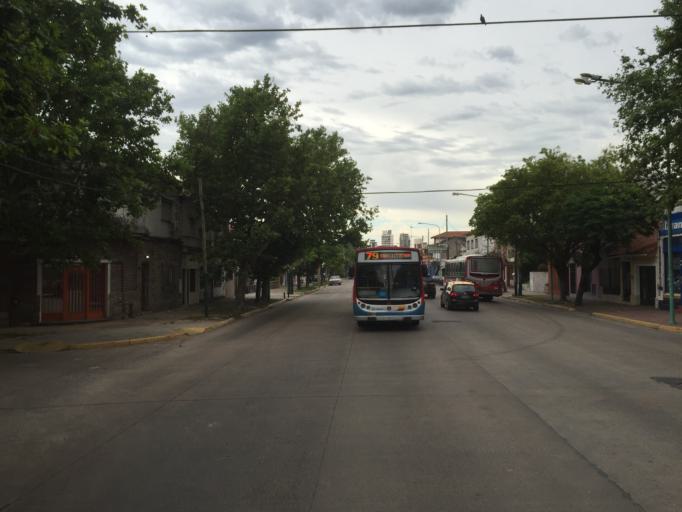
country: AR
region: Buenos Aires
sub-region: Partido de Lomas de Zamora
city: Lomas de Zamora
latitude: -34.7517
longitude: -58.3947
